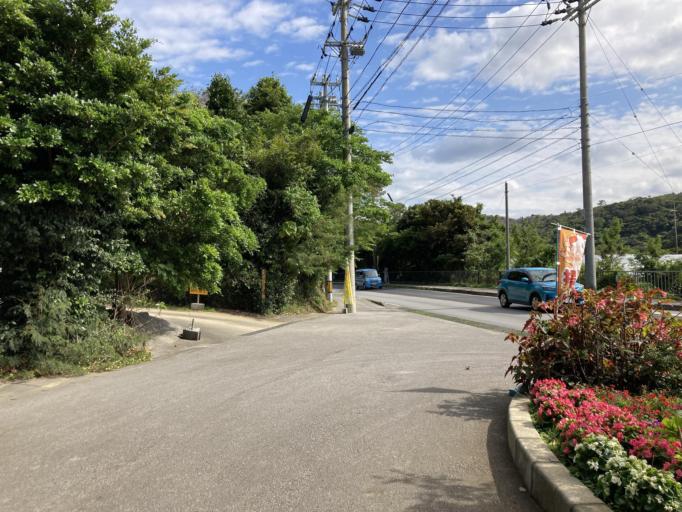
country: JP
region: Okinawa
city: Nago
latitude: 26.6998
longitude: 127.9302
